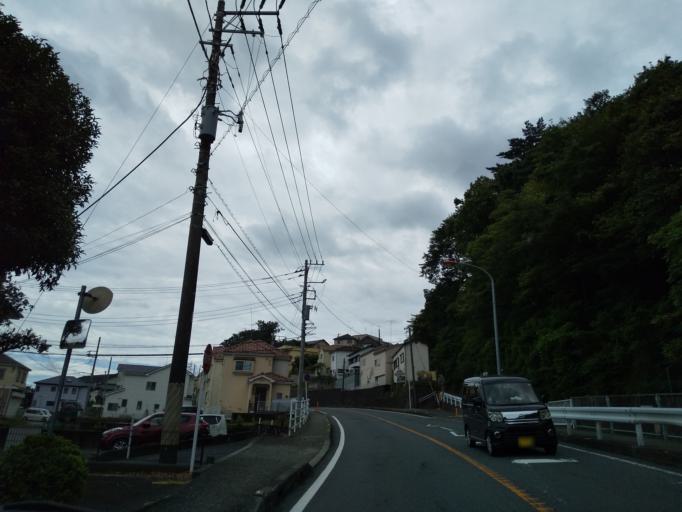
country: JP
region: Kanagawa
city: Zama
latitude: 35.5134
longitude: 139.3626
